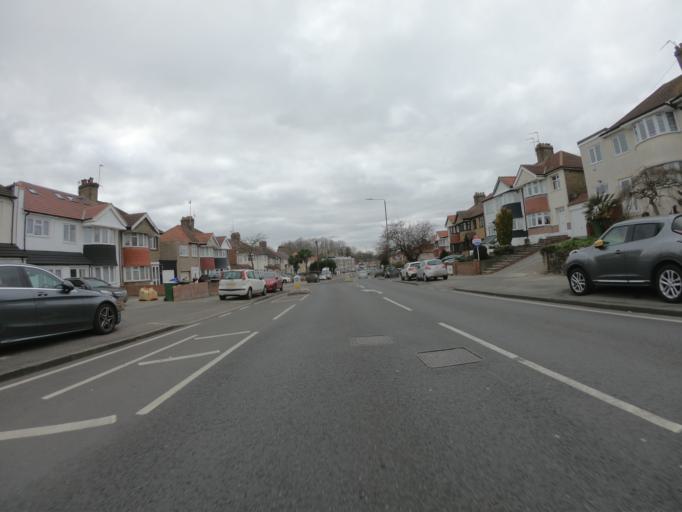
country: GB
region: England
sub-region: Greater London
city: Welling
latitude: 51.4720
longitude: 0.1154
